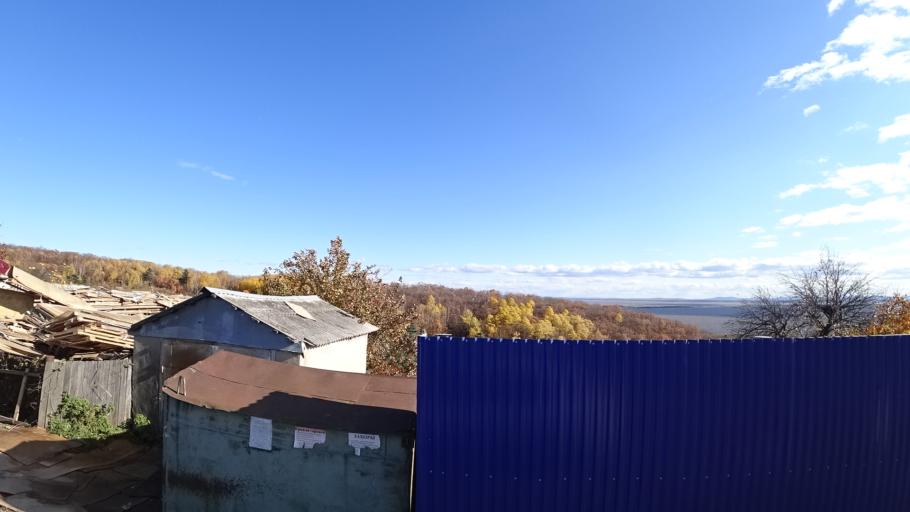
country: RU
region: Khabarovsk Krai
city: Amursk
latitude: 50.2328
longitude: 136.9202
